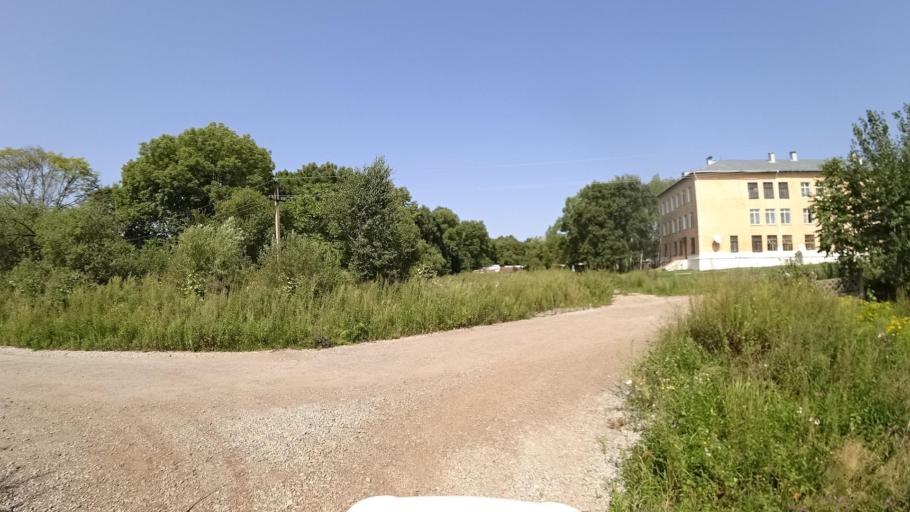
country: RU
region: Khabarovsk Krai
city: Khor
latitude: 47.9637
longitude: 135.1146
